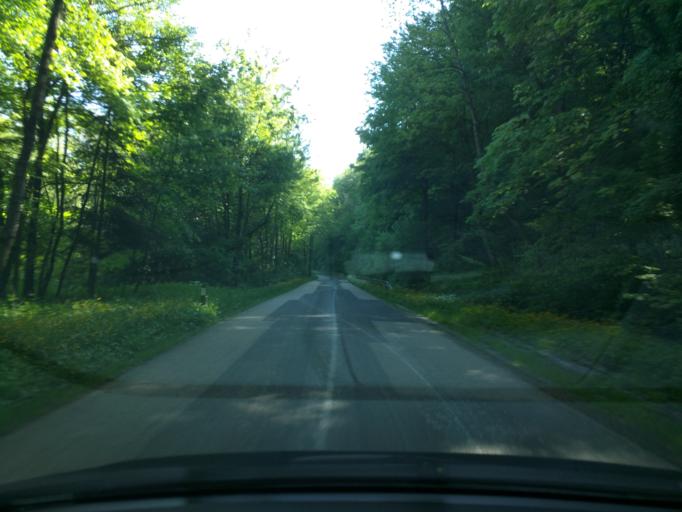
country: AT
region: Lower Austria
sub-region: Politischer Bezirk Amstetten
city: Euratsfeld
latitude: 48.0985
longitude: 14.9463
